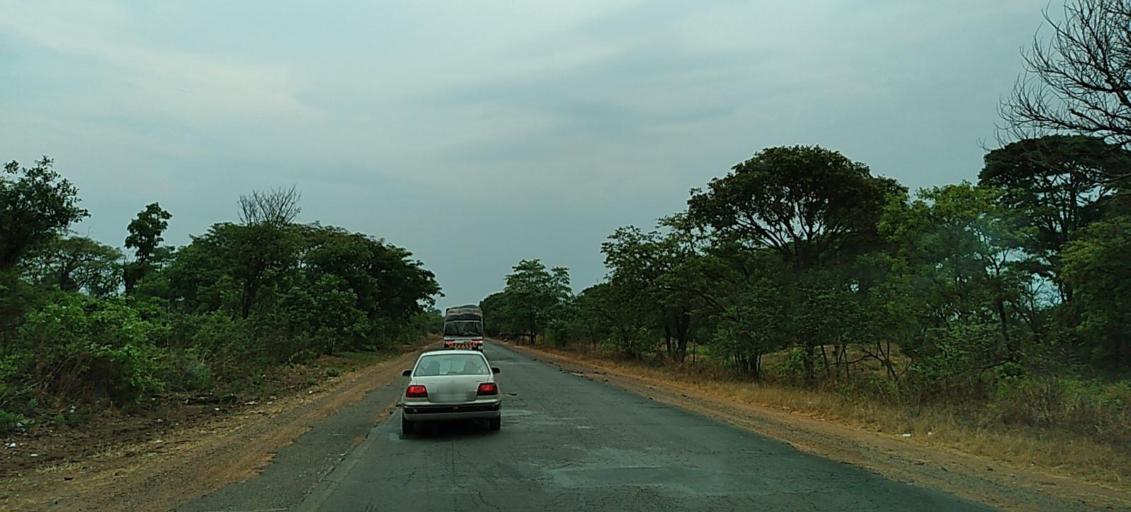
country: ZM
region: Copperbelt
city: Luanshya
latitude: -13.0878
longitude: 28.4363
